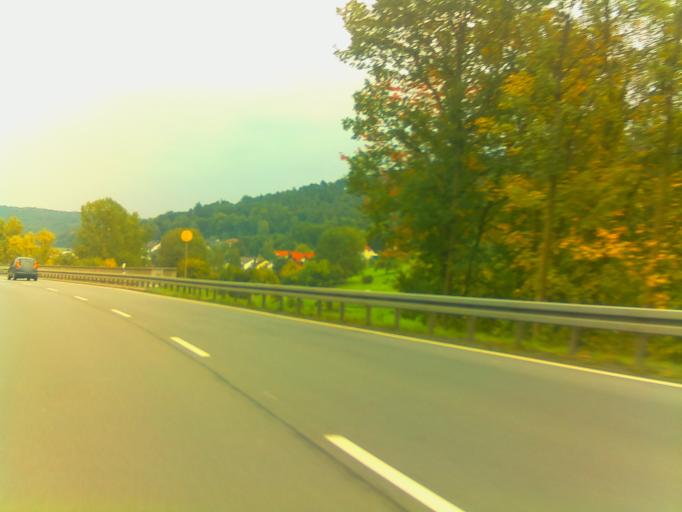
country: DE
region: Hesse
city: Hochst im Odenwald
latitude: 49.8148
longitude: 9.0284
